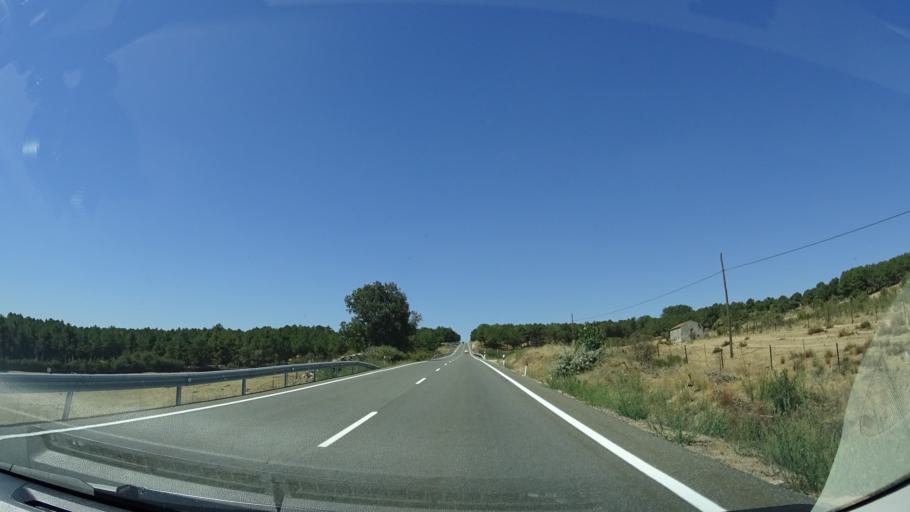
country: ES
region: Castille and Leon
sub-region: Provincia de Avila
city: Navalperal de Pinares
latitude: 40.5918
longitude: -4.3870
